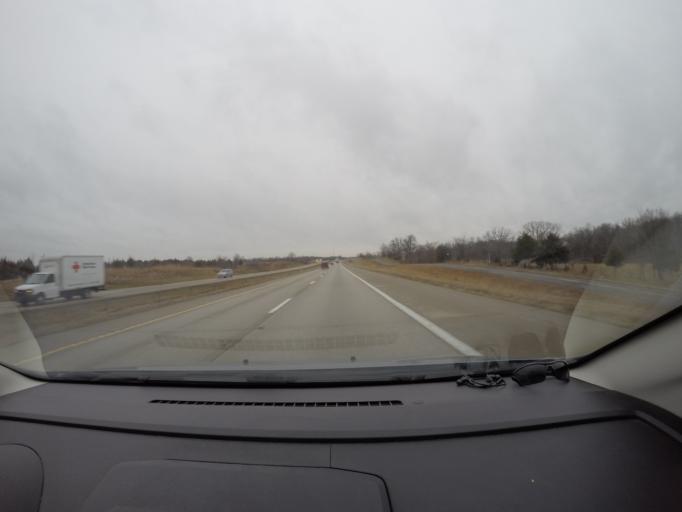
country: US
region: Missouri
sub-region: Montgomery County
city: Montgomery City
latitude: 38.9107
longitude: -91.6695
